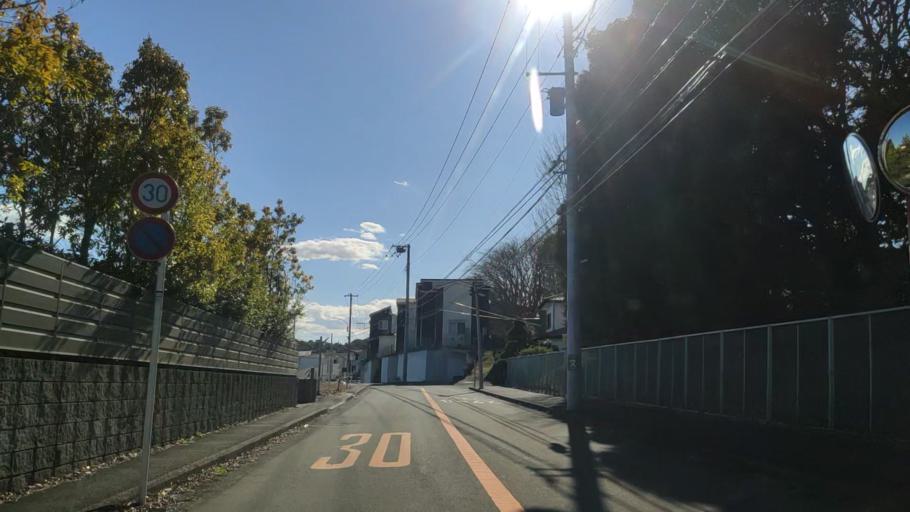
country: JP
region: Kanagawa
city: Minami-rinkan
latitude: 35.5104
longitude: 139.5265
